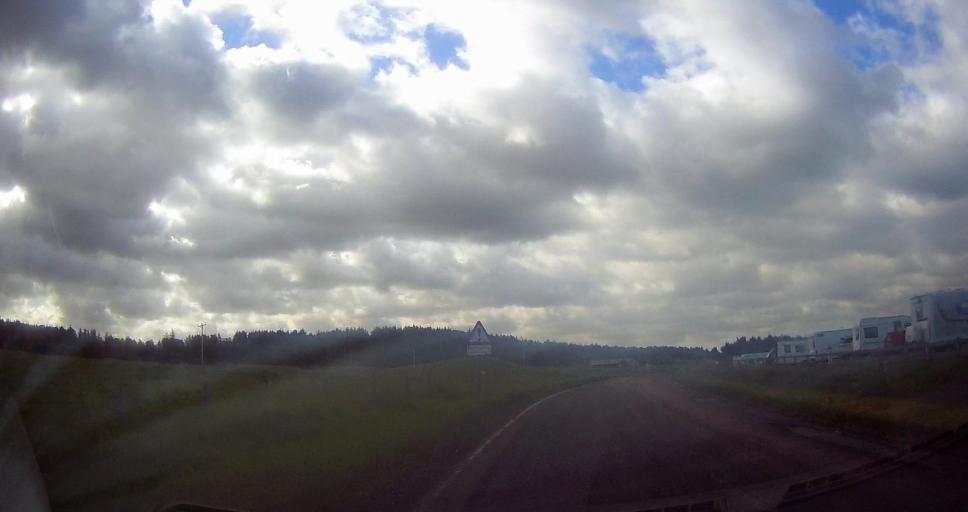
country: GB
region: Scotland
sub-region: Highland
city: Thurso
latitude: 58.6155
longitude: -3.3445
